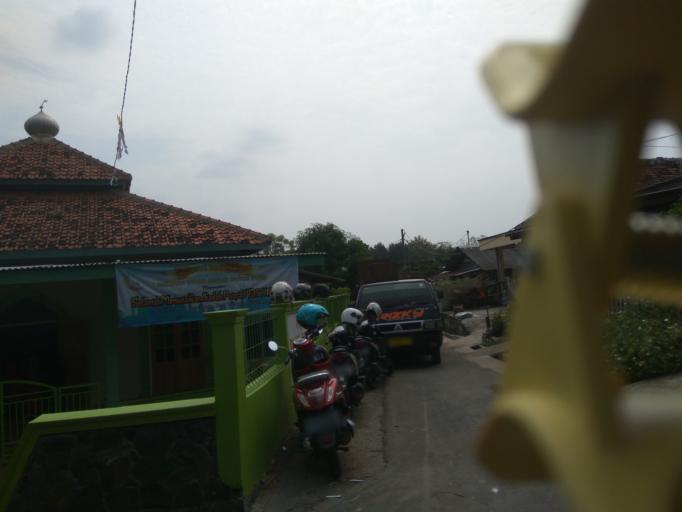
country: ID
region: Central Java
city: Semarang
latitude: -7.0433
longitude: 110.4128
